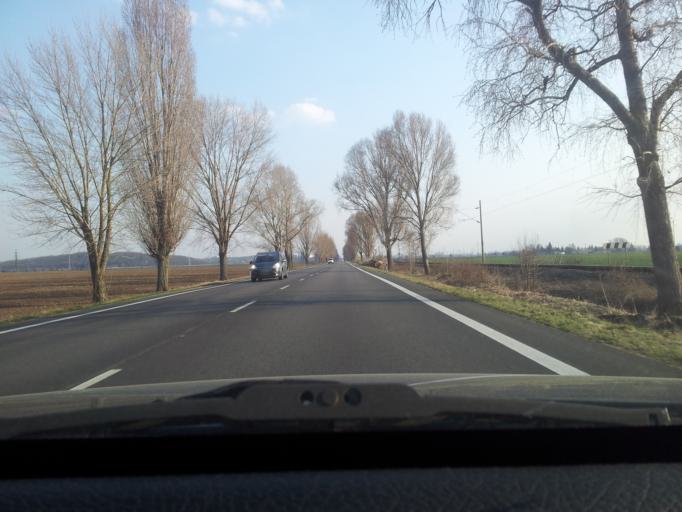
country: SK
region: Nitriansky
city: Levice
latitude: 48.2556
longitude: 18.5765
